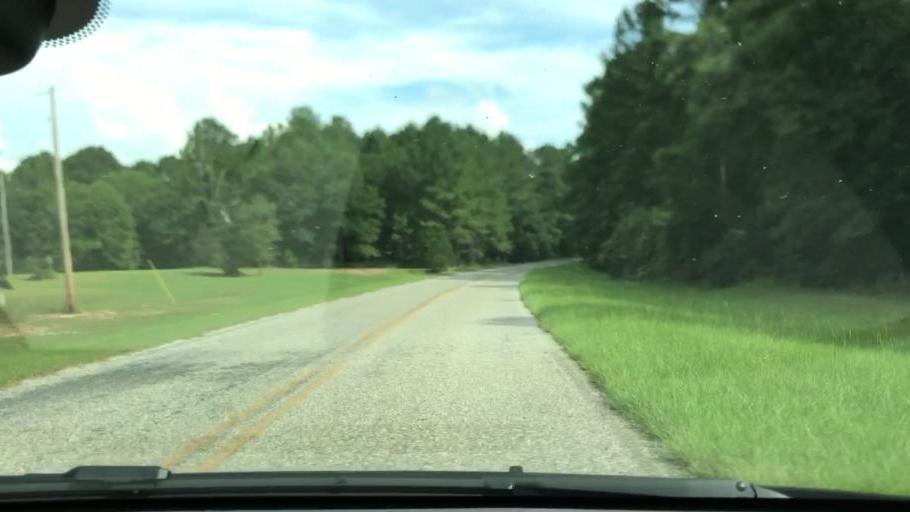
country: US
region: Georgia
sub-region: Early County
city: Blakely
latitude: 31.5040
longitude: -84.9448
